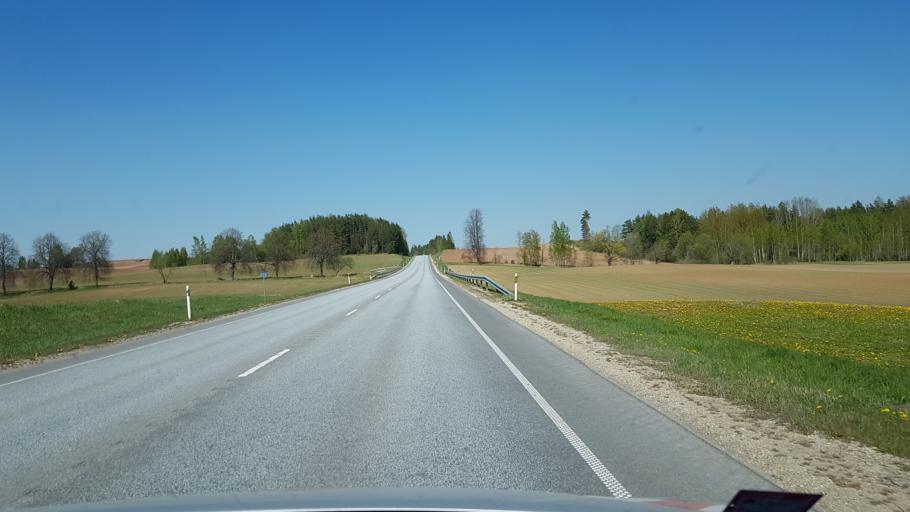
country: EE
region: Tartu
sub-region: UElenurme vald
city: Ulenurme
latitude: 58.1939
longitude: 26.6984
